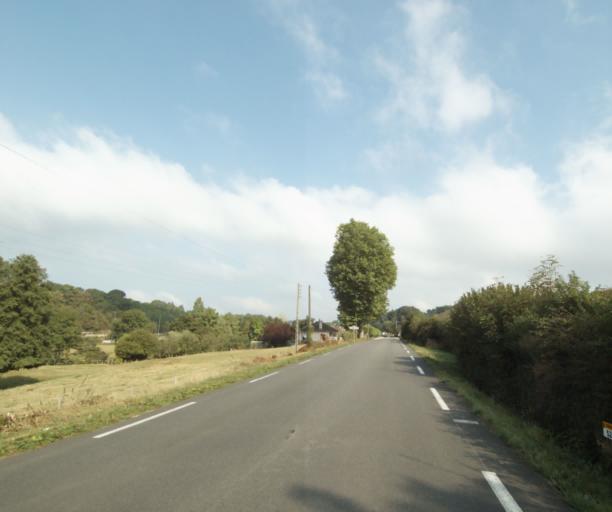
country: FR
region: Bourgogne
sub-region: Departement de Saone-et-Loire
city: Charolles
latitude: 46.4265
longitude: 4.2756
